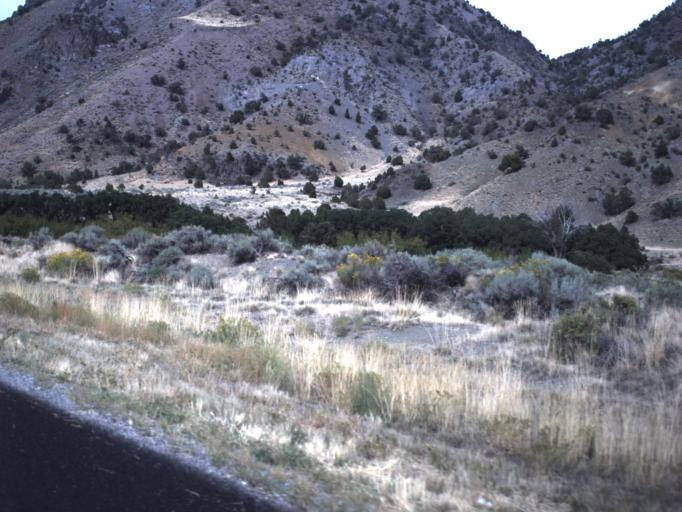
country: US
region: Utah
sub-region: Sevier County
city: Monroe
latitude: 38.5243
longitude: -112.2657
